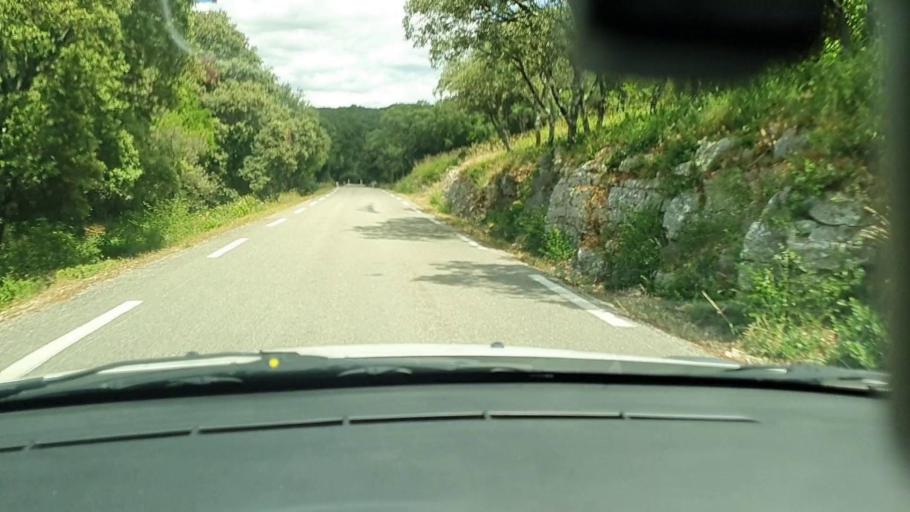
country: FR
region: Languedoc-Roussillon
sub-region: Departement du Gard
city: Cabrieres
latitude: 43.9294
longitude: 4.4734
